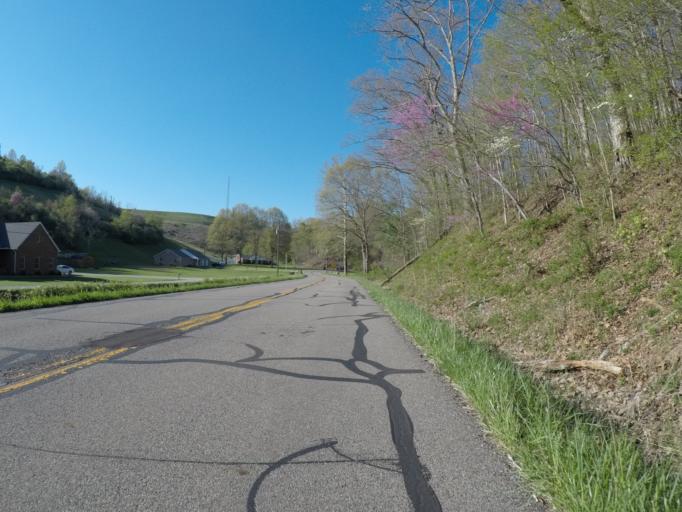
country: US
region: Kentucky
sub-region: Boyd County
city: Meads
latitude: 38.3624
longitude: -82.6886
